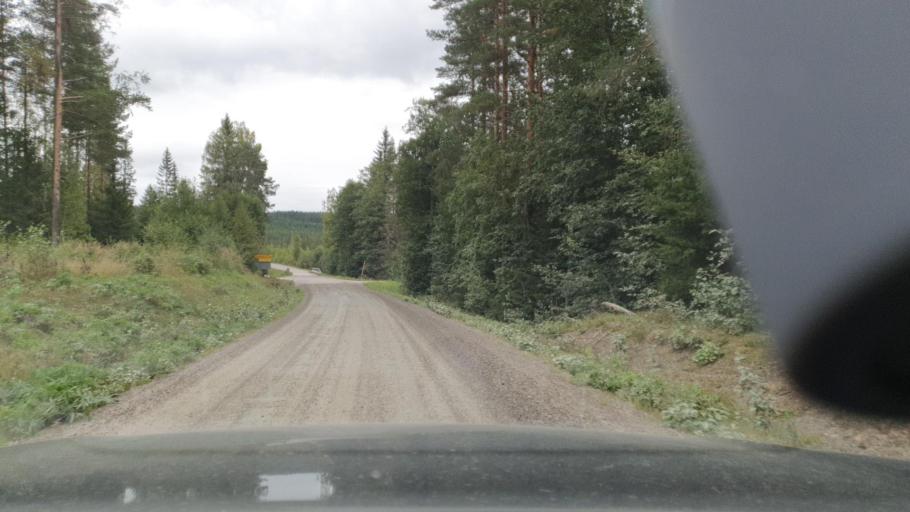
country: SE
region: Vaermland
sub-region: Torsby Kommun
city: Torsby
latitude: 60.3856
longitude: 12.9000
